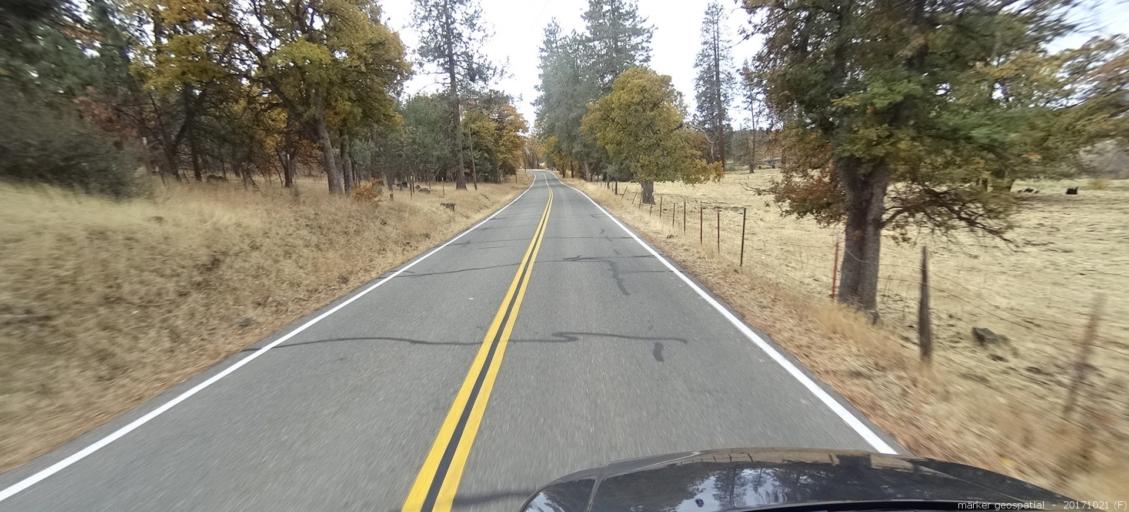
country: US
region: California
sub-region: Shasta County
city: Burney
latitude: 41.0040
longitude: -121.4308
